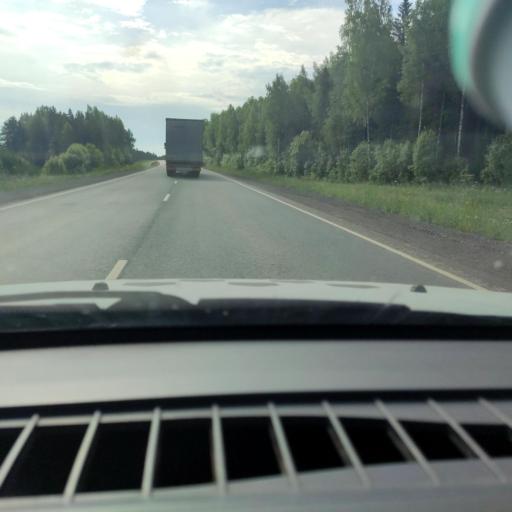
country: RU
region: Perm
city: Siva
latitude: 58.4321
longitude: 54.4409
